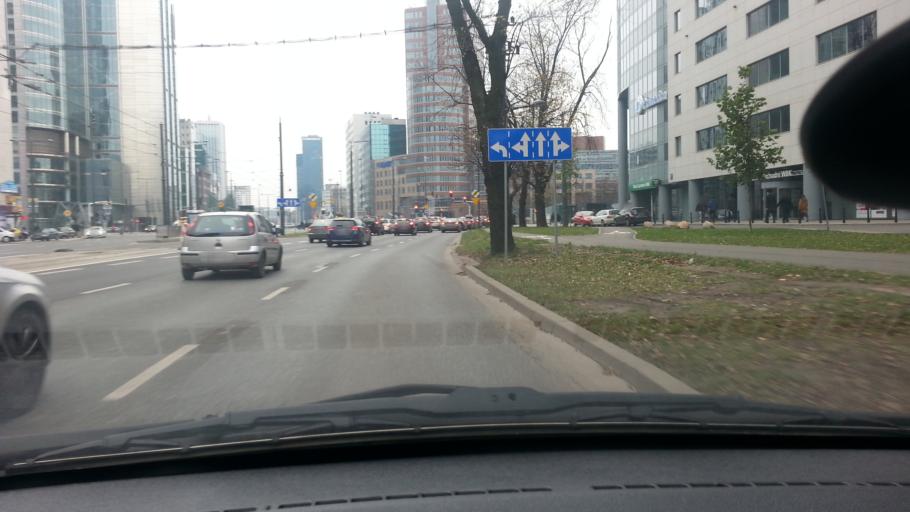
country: PL
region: Masovian Voivodeship
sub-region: Warszawa
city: Wola
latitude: 52.2346
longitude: 20.9976
